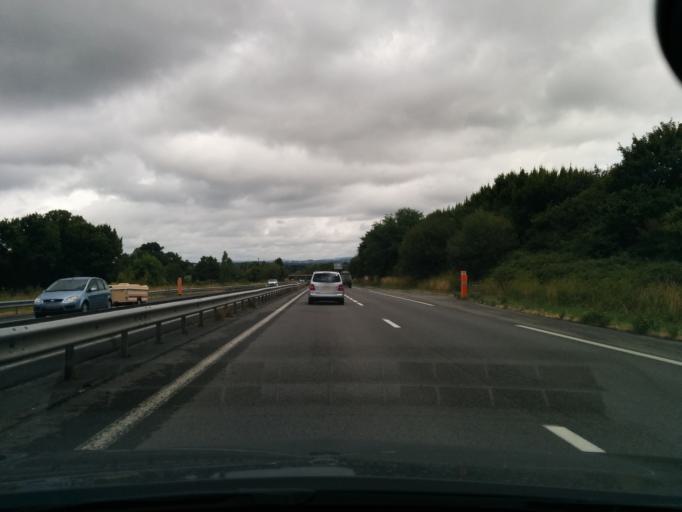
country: FR
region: Limousin
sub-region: Departement de la Correze
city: Uzerche
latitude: 45.4763
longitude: 1.5249
